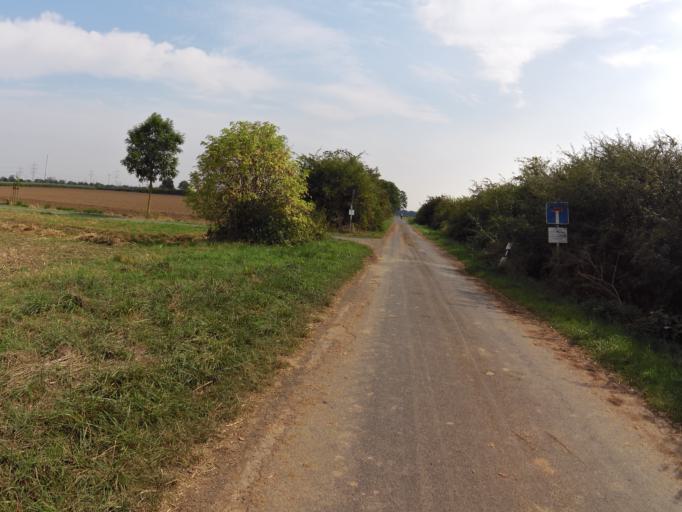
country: DE
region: Lower Saxony
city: Stolzenau
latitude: 52.5298
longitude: 9.0790
